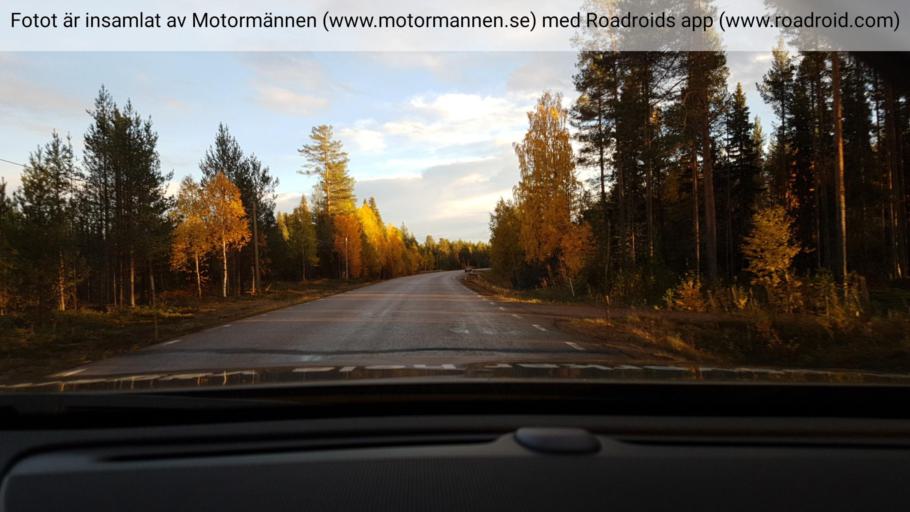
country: SE
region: Norrbotten
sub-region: Overkalix Kommun
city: OEverkalix
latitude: 66.6210
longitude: 22.7463
